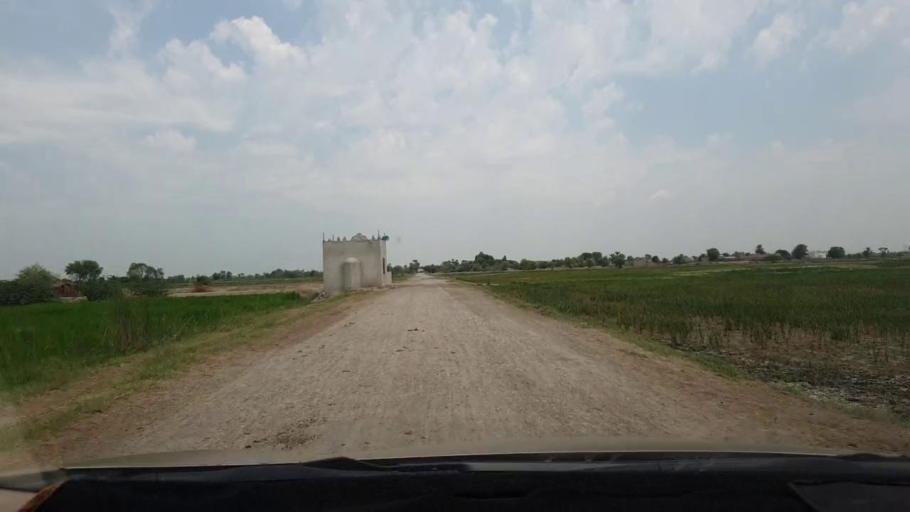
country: PK
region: Sindh
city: Naudero
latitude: 27.7281
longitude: 68.3459
